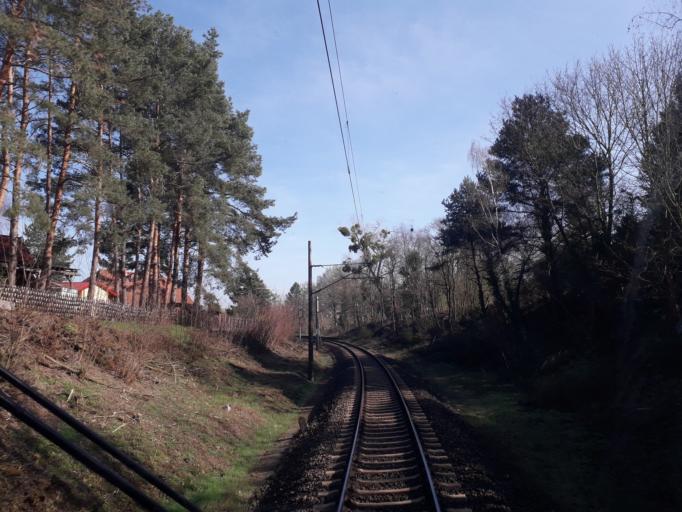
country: DE
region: Brandenburg
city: Michendorf
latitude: 52.3388
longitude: 12.9791
